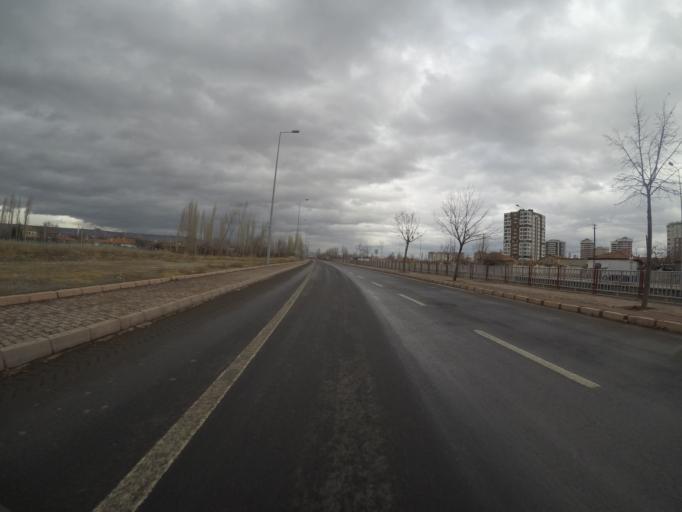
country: TR
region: Kayseri
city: Kayseri
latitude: 38.7513
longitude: 35.4757
